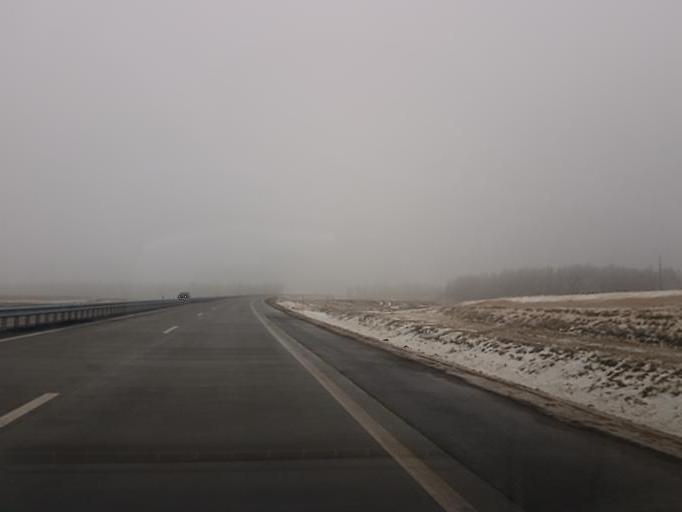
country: BY
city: Fanipol
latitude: 53.7635
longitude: 27.3800
